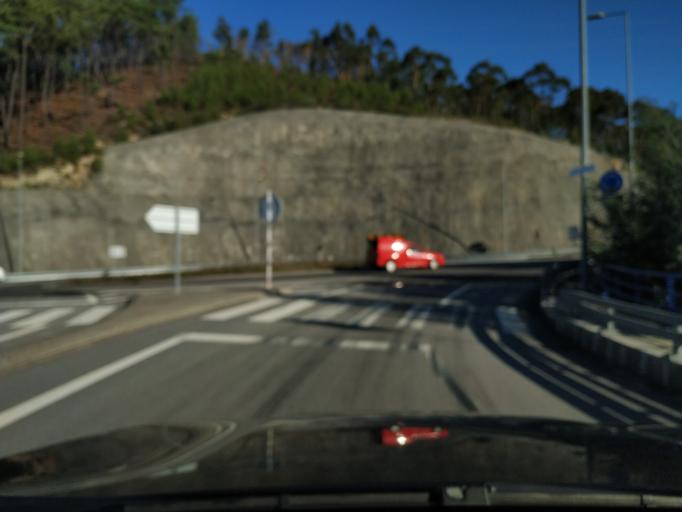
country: PT
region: Aveiro
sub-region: Oliveira de Azemeis
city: Vila Cha
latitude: 40.8780
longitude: -8.4294
